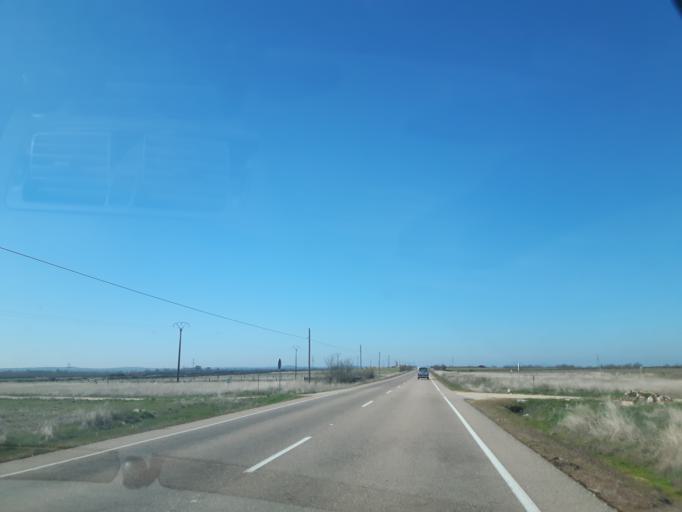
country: ES
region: Castille and Leon
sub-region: Provincia de Salamanca
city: Lumbrales
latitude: 40.9492
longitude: -6.6807
